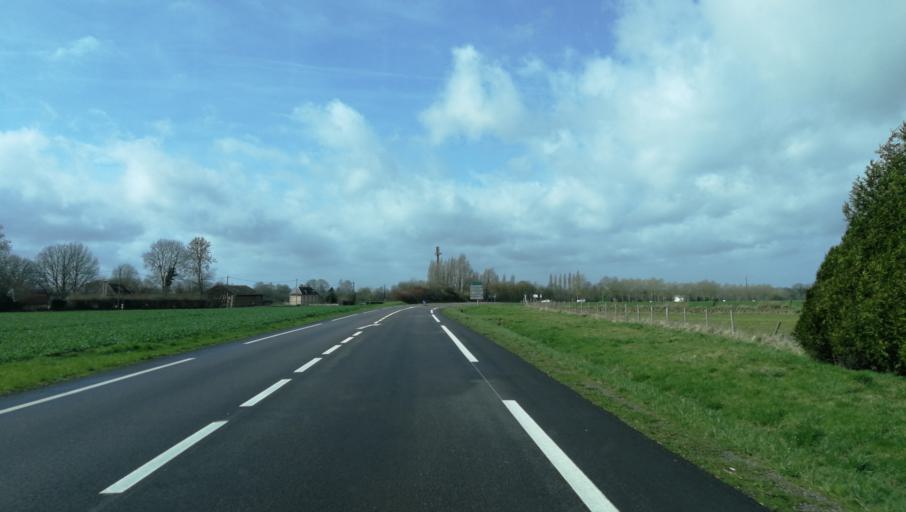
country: FR
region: Haute-Normandie
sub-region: Departement de l'Eure
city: Epaignes
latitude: 49.2853
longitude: 0.4093
